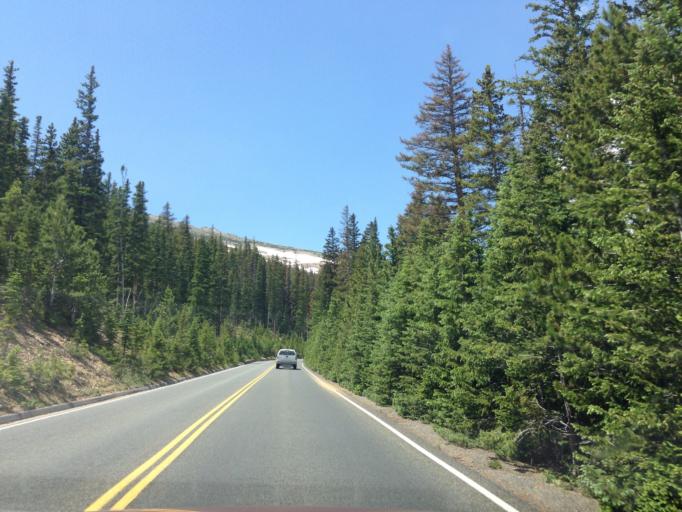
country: US
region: Colorado
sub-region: Larimer County
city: Estes Park
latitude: 40.3868
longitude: -105.6548
